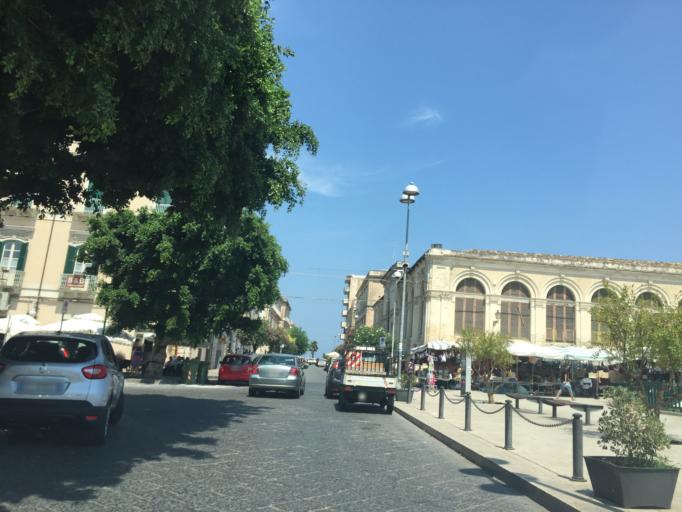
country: IT
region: Sicily
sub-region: Provincia di Siracusa
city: Siracusa
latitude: 37.0641
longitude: 15.2925
